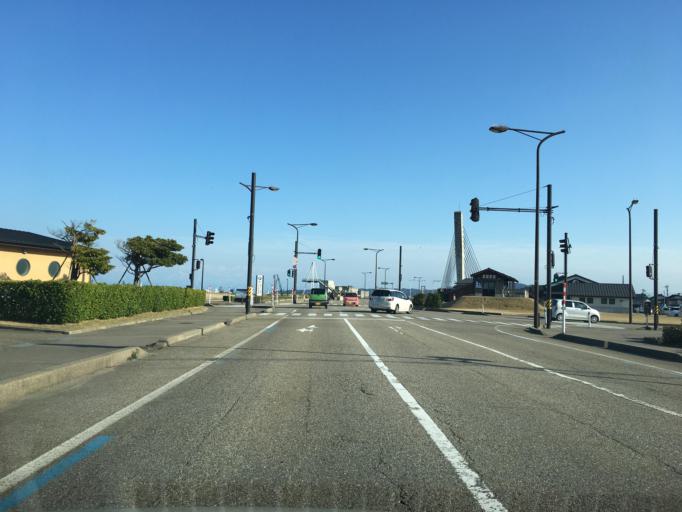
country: JP
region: Toyama
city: Himi
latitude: 36.8660
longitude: 136.9865
